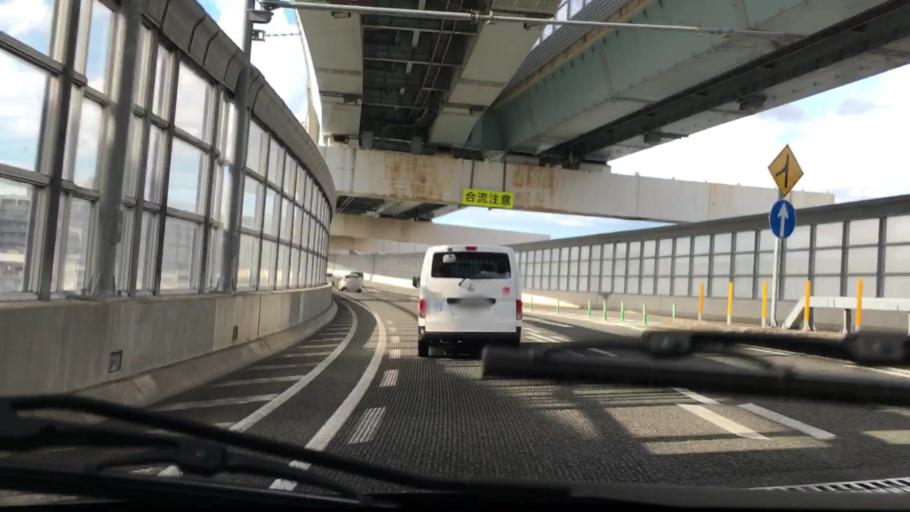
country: JP
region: Fukuoka
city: Fukuoka-shi
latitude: 33.5700
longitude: 130.3170
